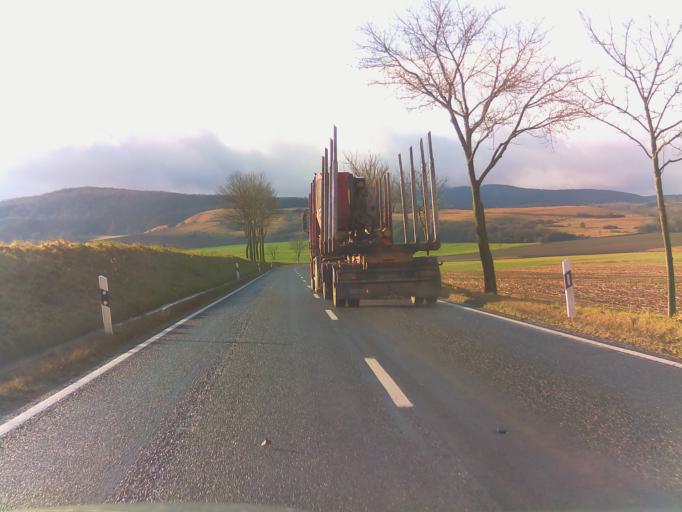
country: DE
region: Thuringia
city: Rosa
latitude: 50.7081
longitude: 10.2448
